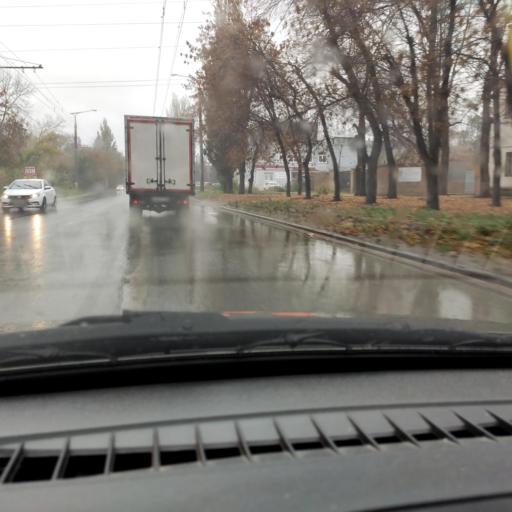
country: RU
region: Samara
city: Tol'yatti
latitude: 53.5645
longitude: 49.4562
